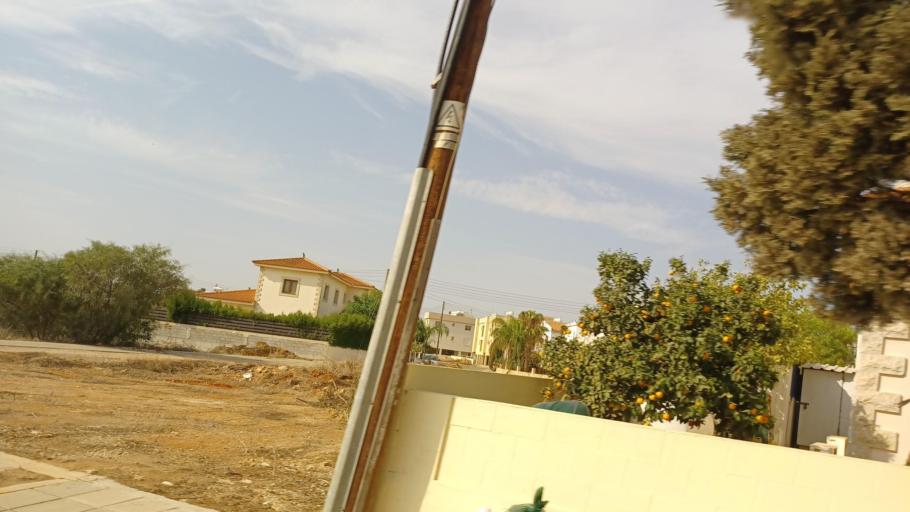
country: CY
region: Ammochostos
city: Liopetri
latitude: 35.0194
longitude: 33.9020
